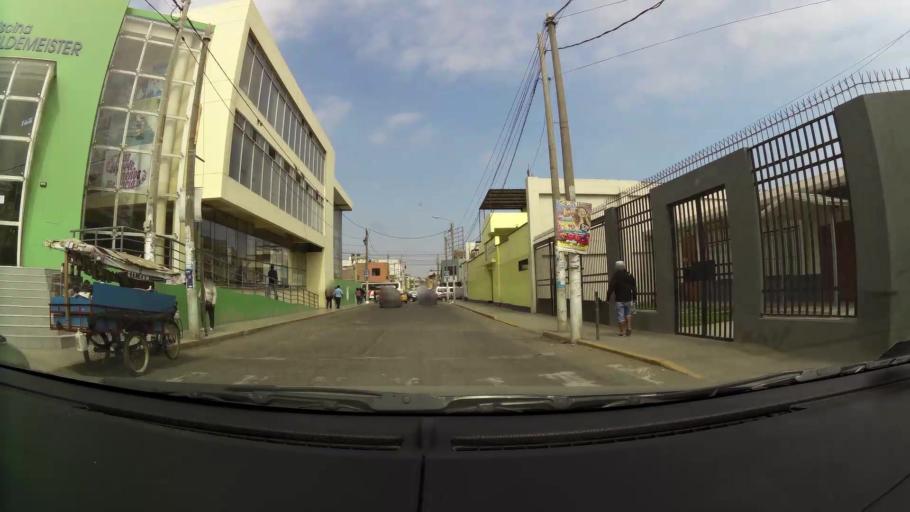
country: PE
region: La Libertad
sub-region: Provincia de Trujillo
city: Trujillo
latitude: -8.1170
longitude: -79.0246
